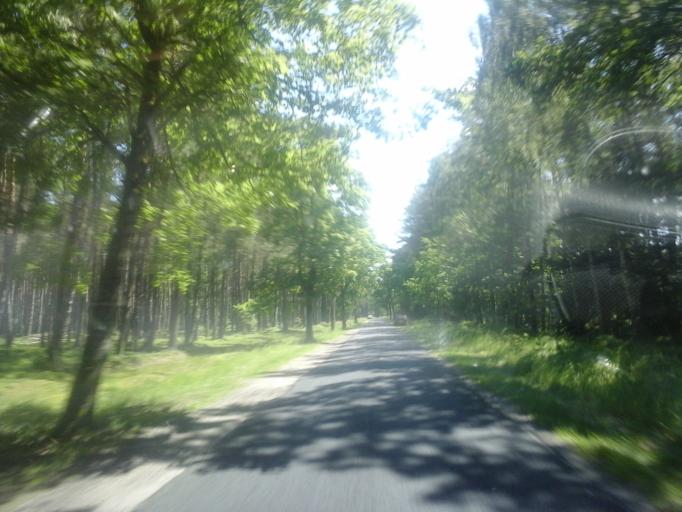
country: PL
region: West Pomeranian Voivodeship
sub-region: Powiat bialogardzki
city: Bialogard
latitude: 54.1032
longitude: 16.0341
